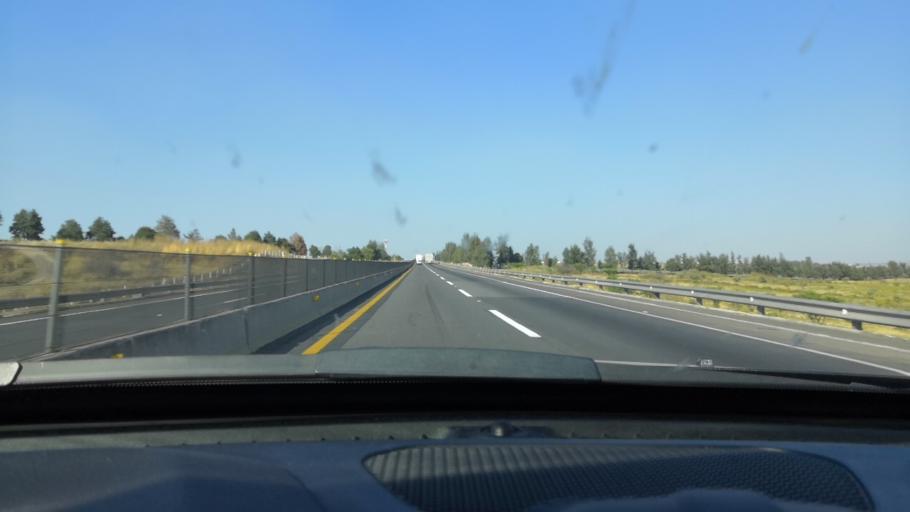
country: MX
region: Jalisco
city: Tepatitlan de Morelos
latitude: 20.7941
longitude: -102.8188
